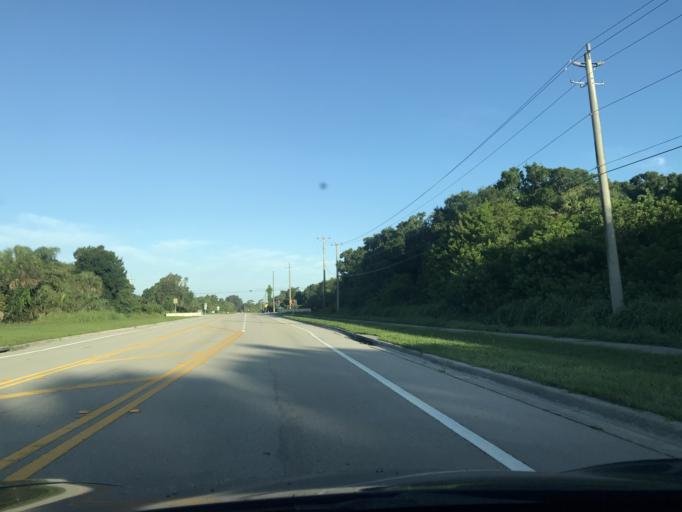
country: US
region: Florida
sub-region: Indian River County
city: West Vero Corridor
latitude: 27.6608
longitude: -80.4615
